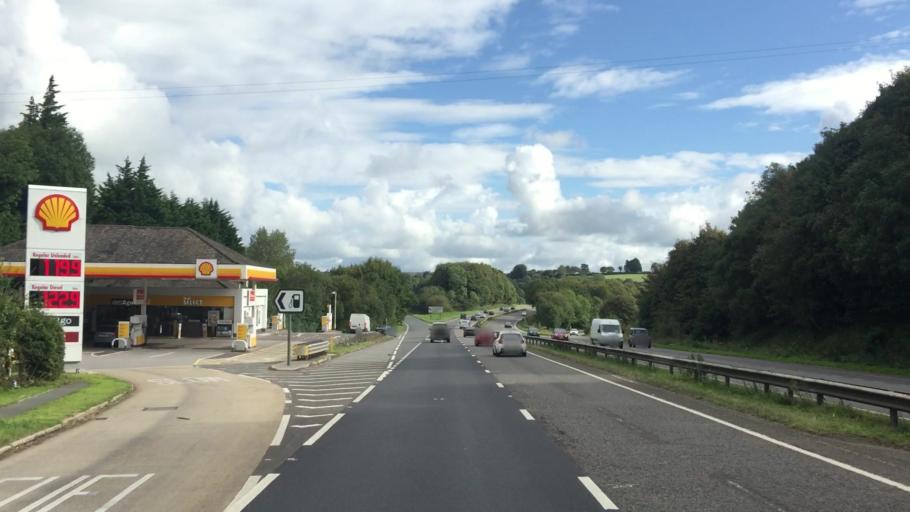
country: GB
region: England
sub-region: Devon
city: South Brent
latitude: 50.4145
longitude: -3.8433
